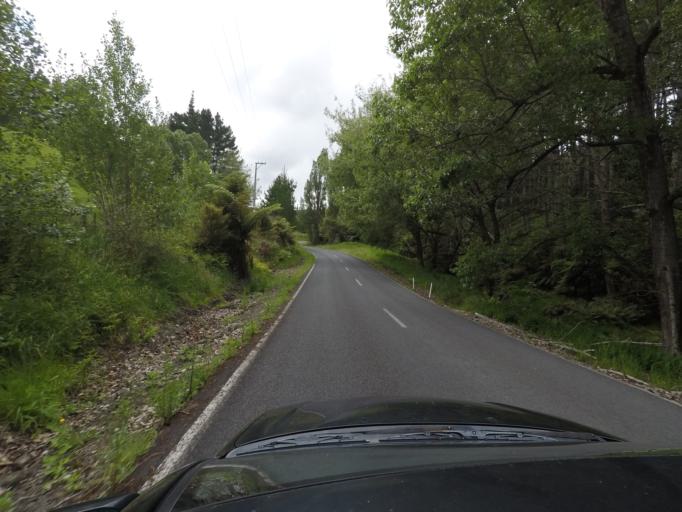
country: NZ
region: Auckland
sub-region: Auckland
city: Warkworth
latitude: -36.4989
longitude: 174.6278
